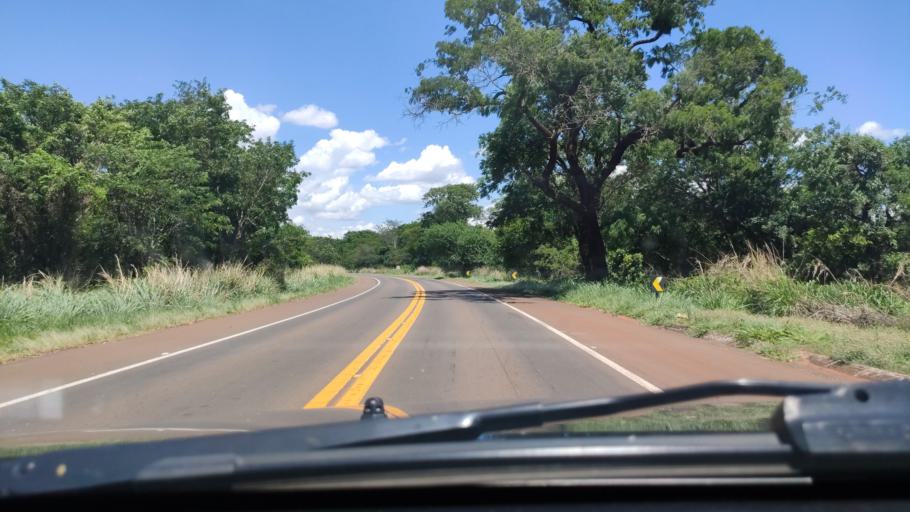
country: BR
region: Sao Paulo
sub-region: Boa Esperanca Do Sul
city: Boa Esperanca do Sul
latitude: -22.0693
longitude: -48.3680
